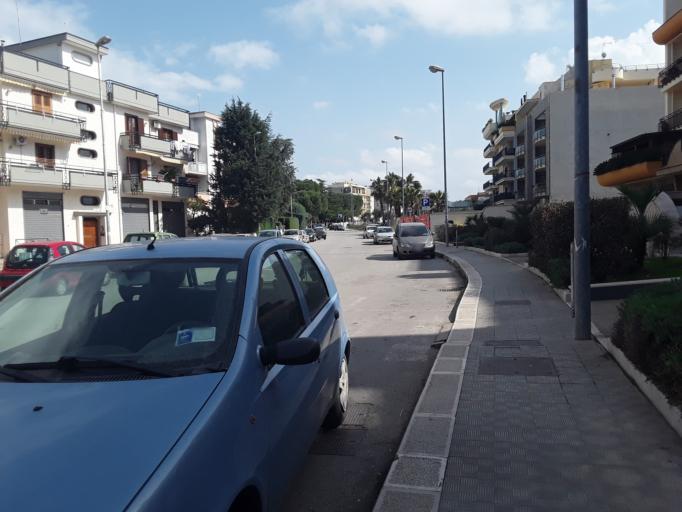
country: IT
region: Apulia
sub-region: Provincia di Bari
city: Ruvo di Puglia
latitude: 41.1236
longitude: 16.4801
